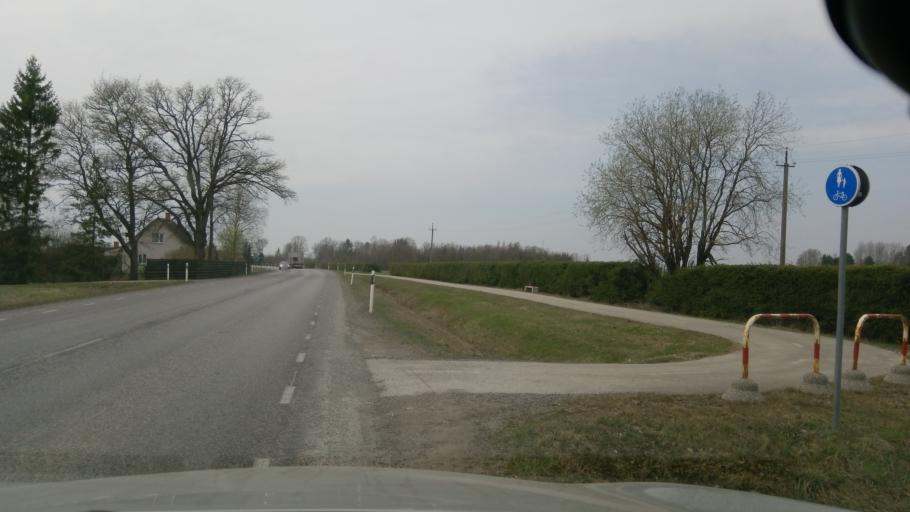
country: EE
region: Jaervamaa
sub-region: Tueri vald
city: Sarevere
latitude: 58.7790
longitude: 25.4617
